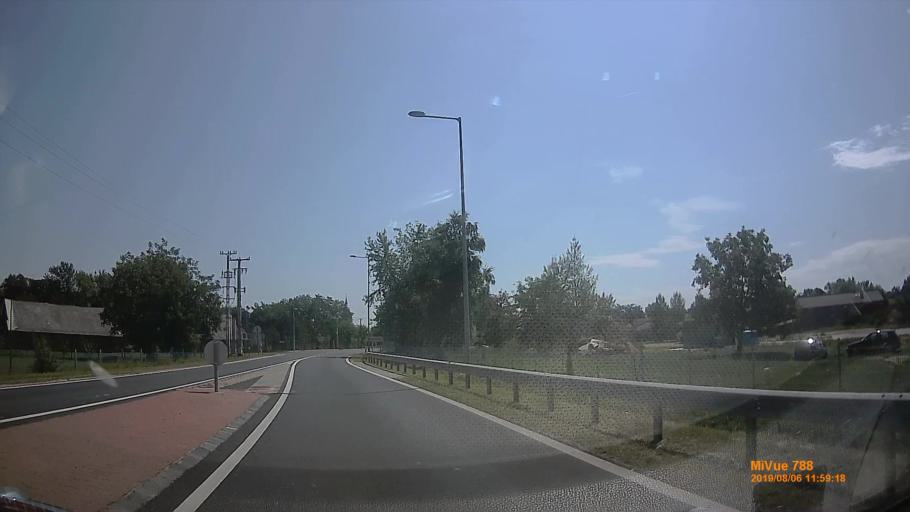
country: HU
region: Vas
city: Vasvar
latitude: 47.0688
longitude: 16.7397
